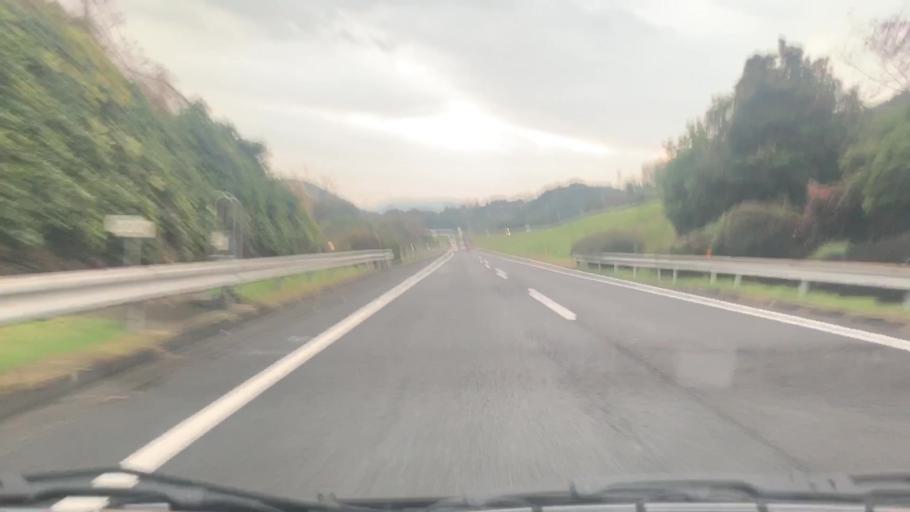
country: JP
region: Nagasaki
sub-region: Isahaya-shi
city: Isahaya
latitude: 32.8662
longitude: 130.0000
